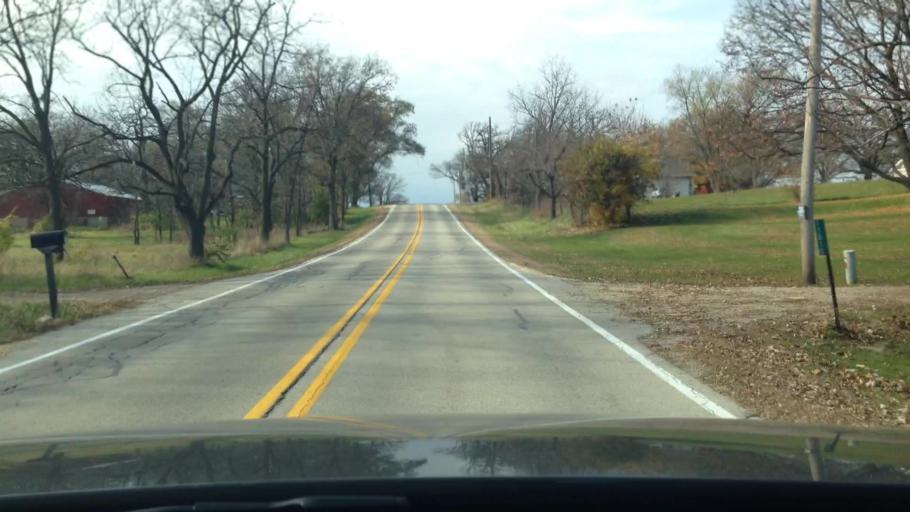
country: US
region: Illinois
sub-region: McHenry County
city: Woodstock
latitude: 42.2984
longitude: -88.4671
